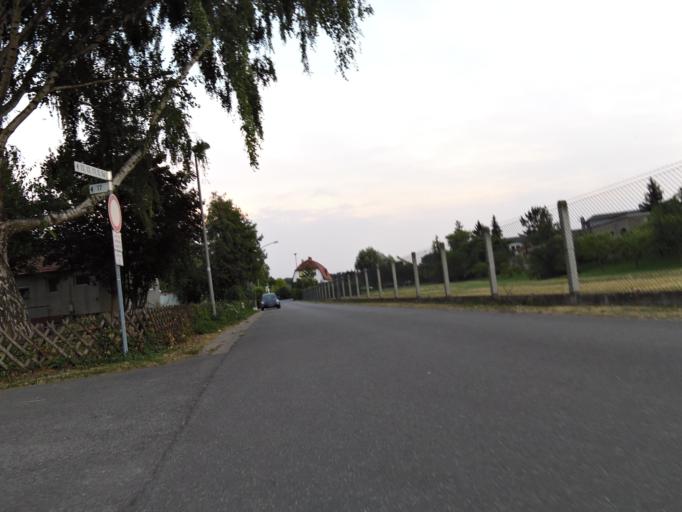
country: DE
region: Rheinland-Pfalz
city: Nierstein
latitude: 49.8678
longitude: 8.3564
